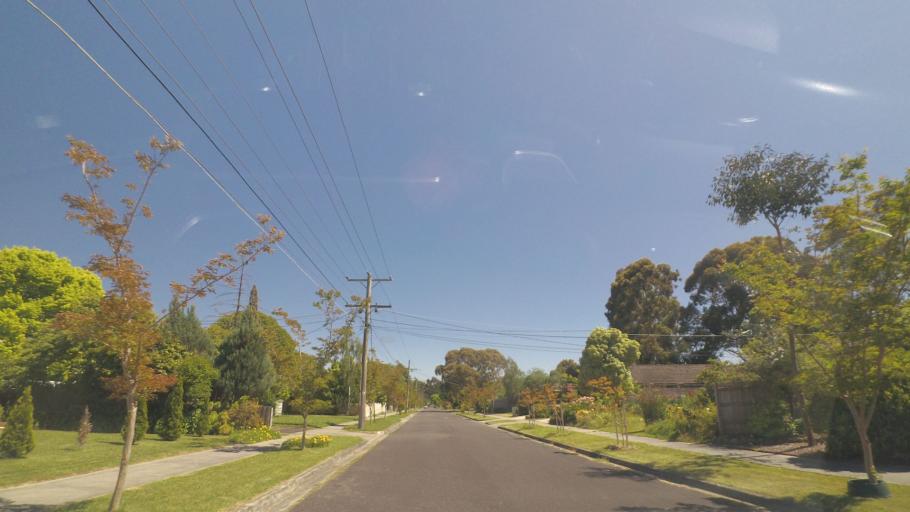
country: AU
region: Victoria
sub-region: Maroondah
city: Croydon Hills
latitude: -37.7876
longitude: 145.2653
